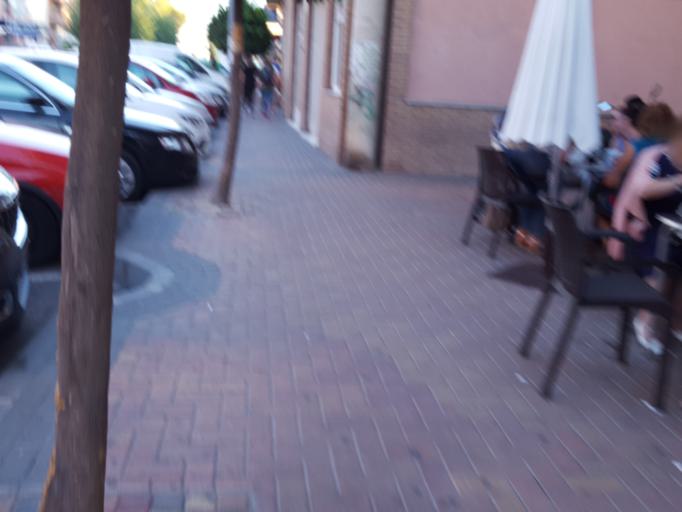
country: ES
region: Murcia
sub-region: Murcia
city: Murcia
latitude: 38.0084
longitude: -1.1517
